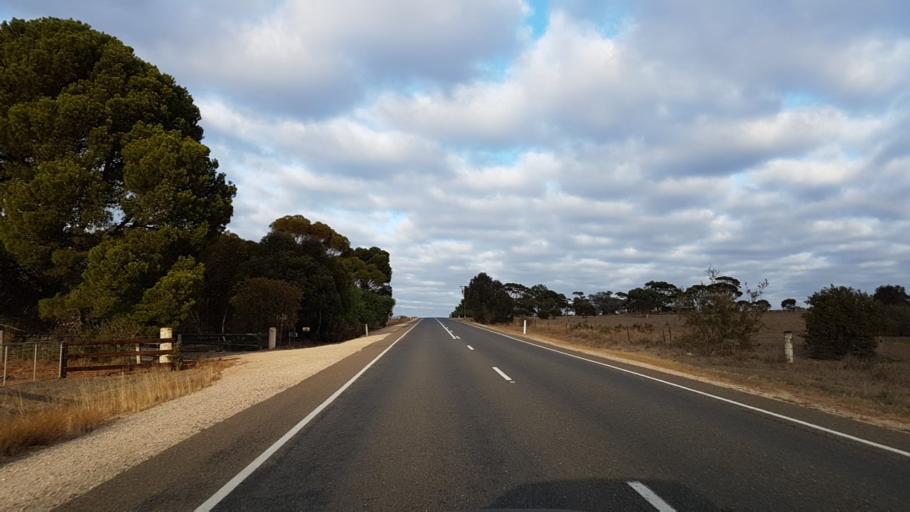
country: AU
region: South Australia
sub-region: Mount Barker
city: Callington
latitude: -35.1853
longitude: 138.9999
